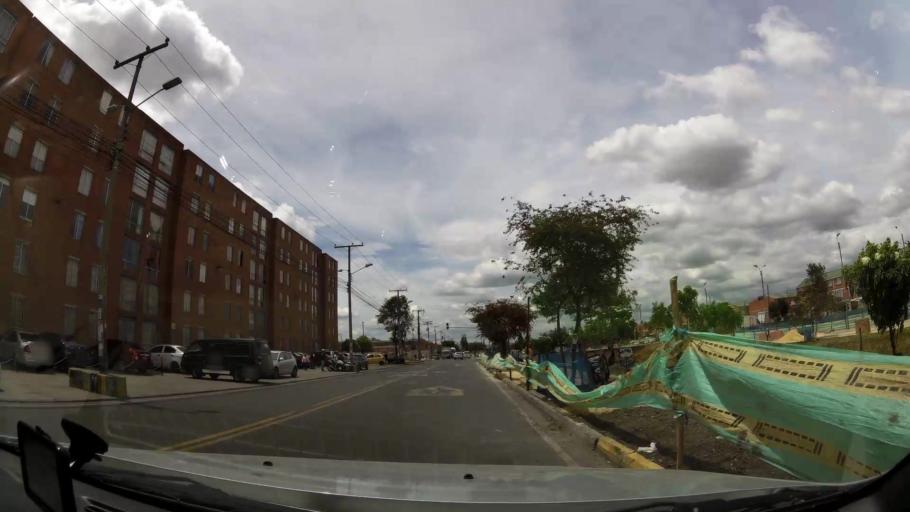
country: CO
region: Bogota D.C.
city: Bogota
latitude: 4.6495
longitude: -74.1571
